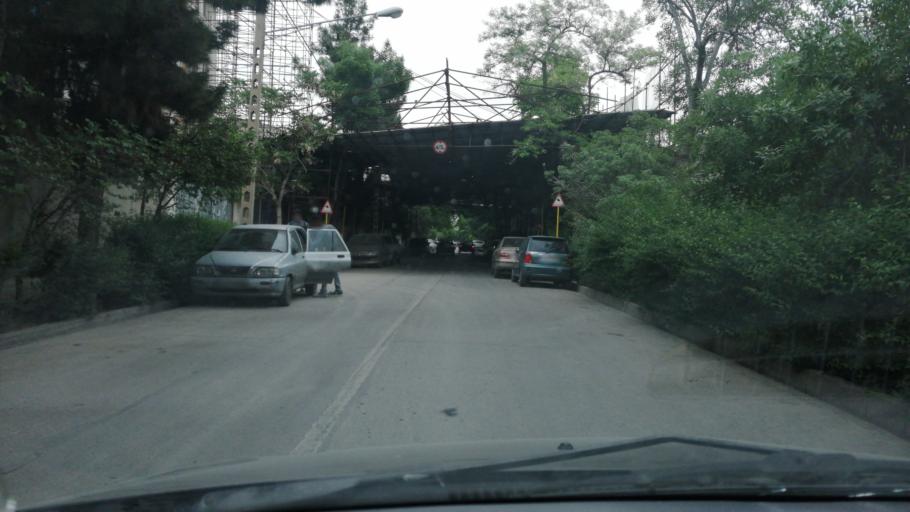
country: IR
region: Razavi Khorasan
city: Mashhad
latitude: 36.2861
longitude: 59.5753
